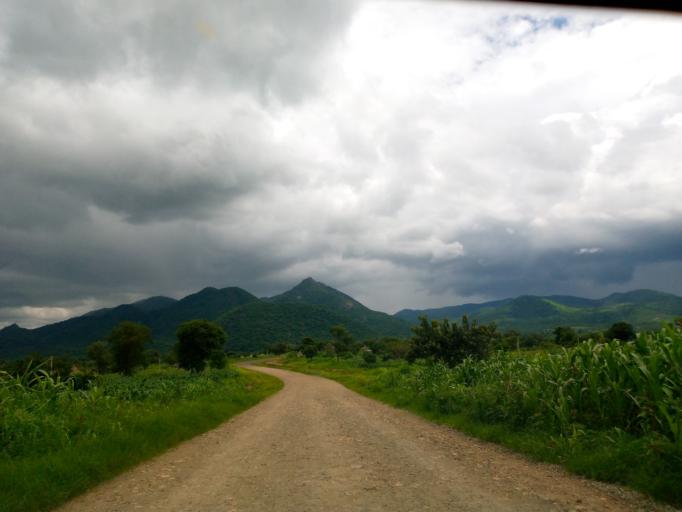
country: ET
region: Oromiya
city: Mendi
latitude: 10.1828
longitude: 35.0928
